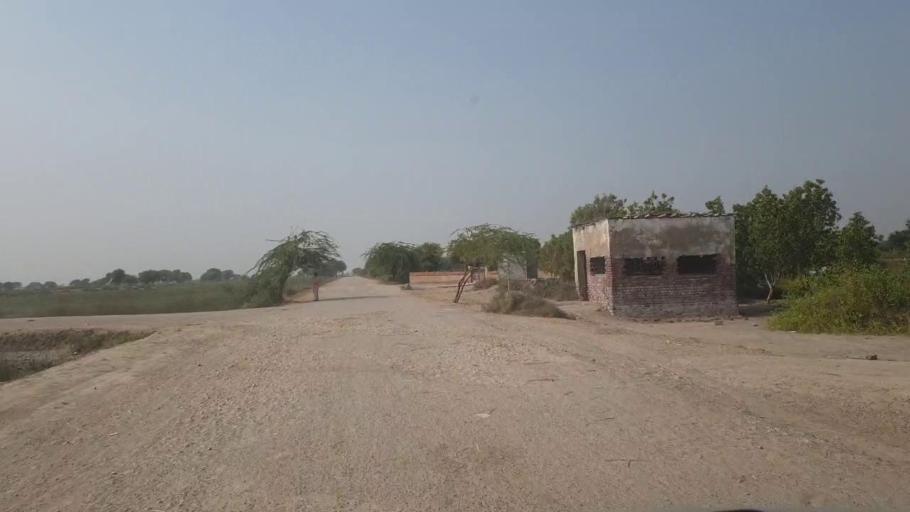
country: PK
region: Sindh
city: Matli
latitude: 25.0213
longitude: 68.6835
